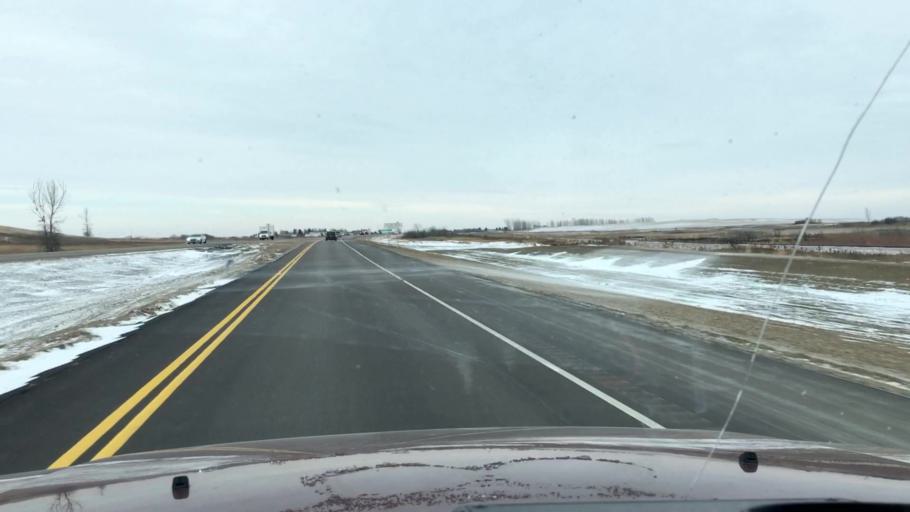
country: CA
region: Saskatchewan
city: Moose Jaw
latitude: 50.8618
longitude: -105.5897
